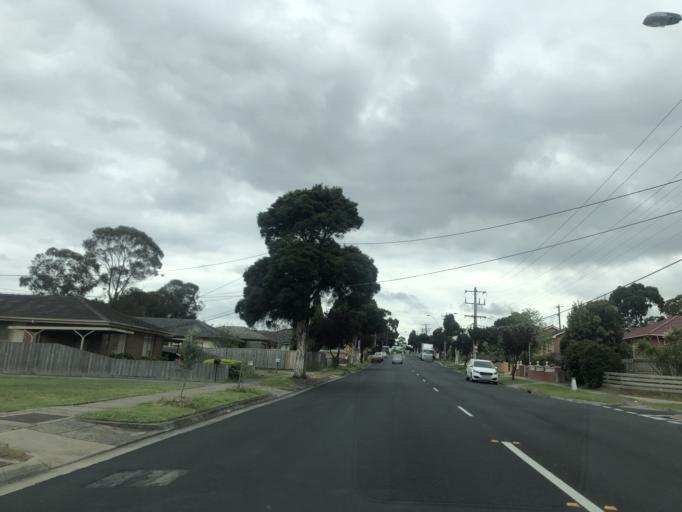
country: AU
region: Victoria
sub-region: Greater Dandenong
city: Noble Park North
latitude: -37.9583
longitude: 145.1913
